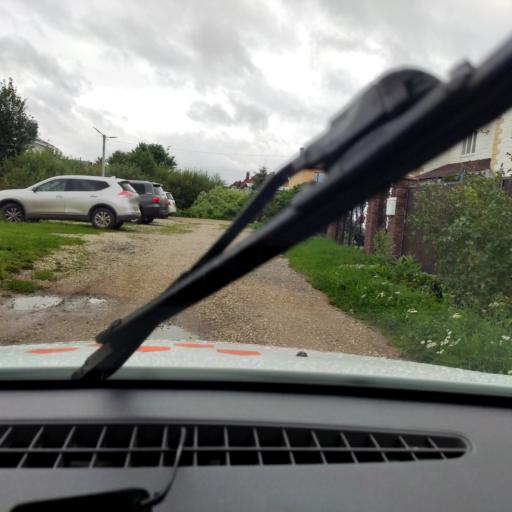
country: RU
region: Bashkortostan
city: Ufa
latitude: 54.6246
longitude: 55.9081
